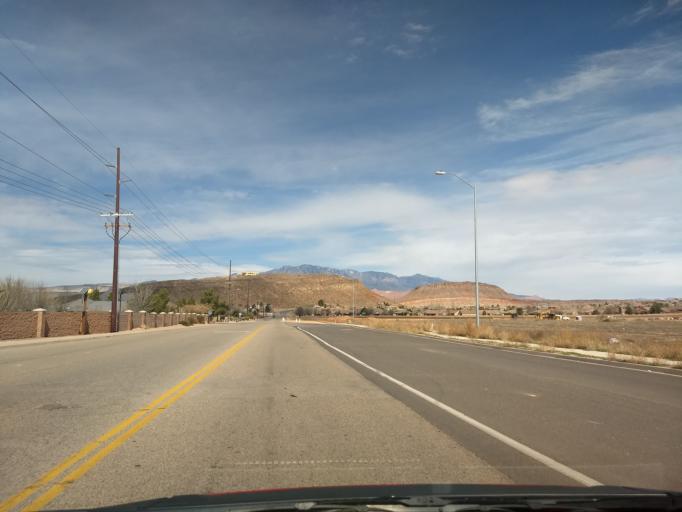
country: US
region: Utah
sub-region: Washington County
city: Washington
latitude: 37.0893
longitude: -113.4997
